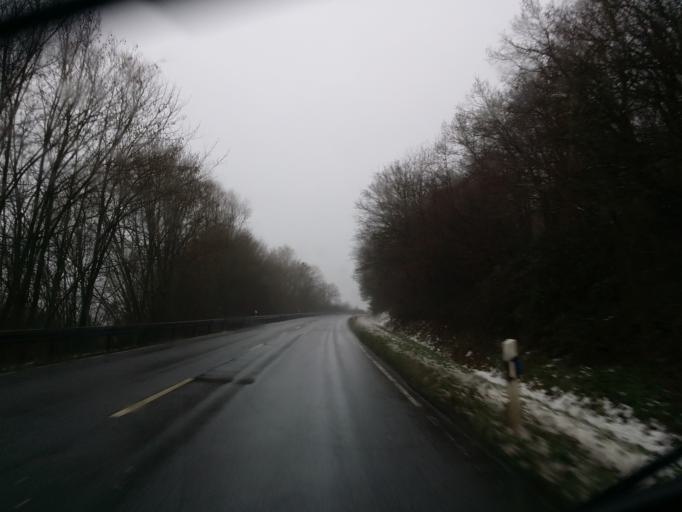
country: DE
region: Hesse
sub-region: Regierungsbezirk Darmstadt
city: Waldems
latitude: 50.2612
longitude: 8.3002
